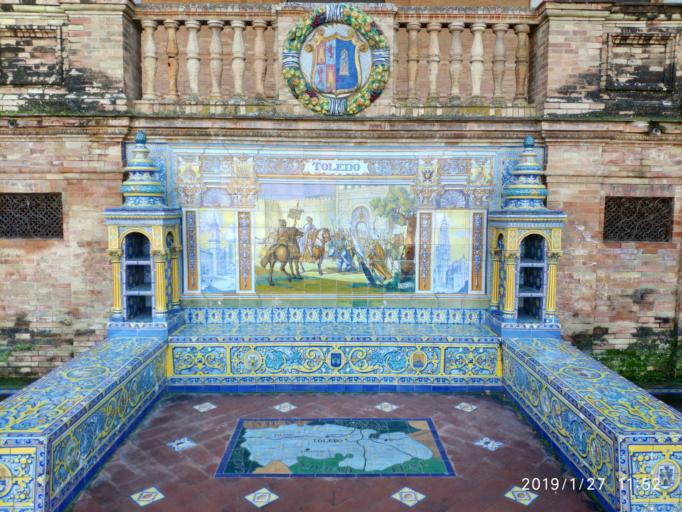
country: ES
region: Andalusia
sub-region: Provincia de Sevilla
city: Sevilla
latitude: 37.3760
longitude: -5.9864
